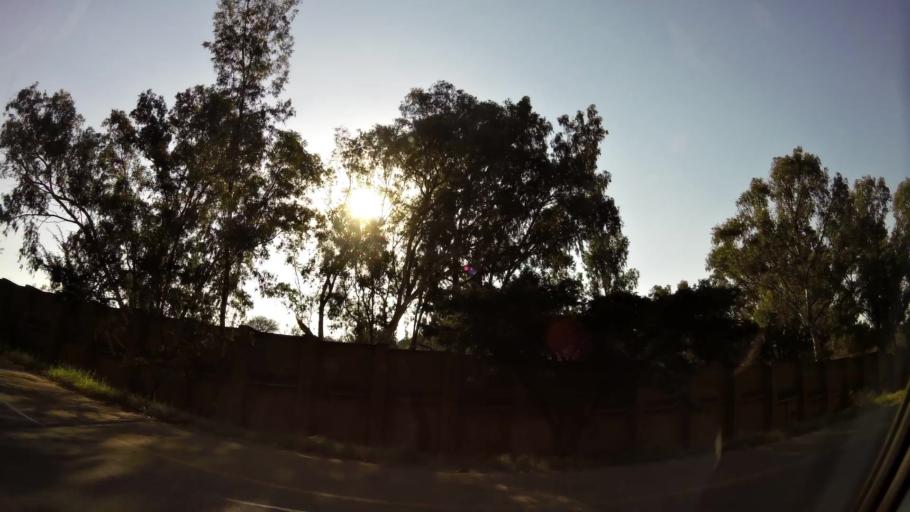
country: ZA
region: Gauteng
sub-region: City of Tshwane Metropolitan Municipality
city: Pretoria
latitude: -25.7828
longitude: 28.3335
